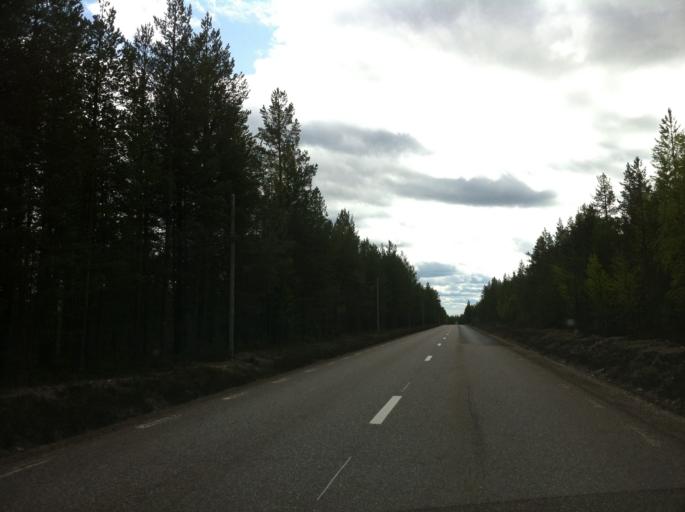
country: NO
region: Hedmark
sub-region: Trysil
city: Innbygda
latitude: 61.6567
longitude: 13.1221
